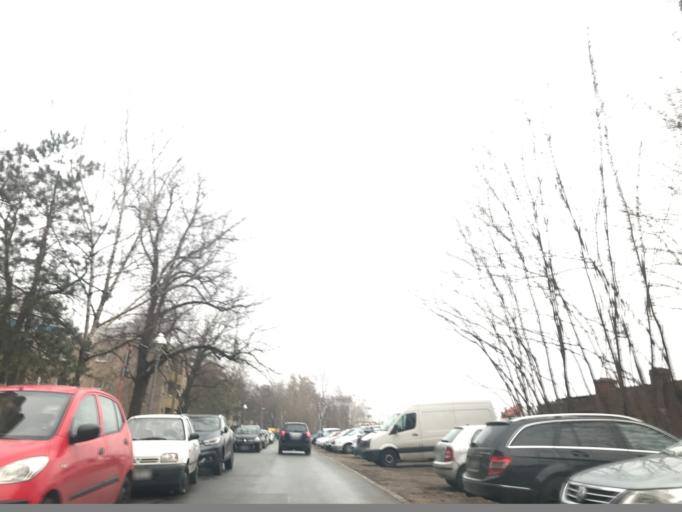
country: DE
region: Berlin
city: Hakenfelde
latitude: 52.5511
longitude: 13.2119
